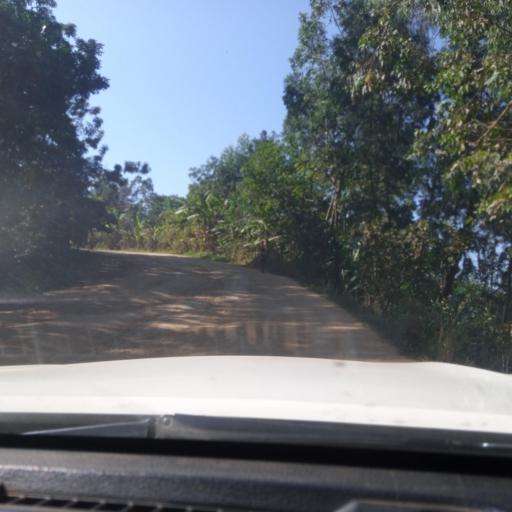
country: ET
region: Southern Nations, Nationalities, and People's Region
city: Mizan Teferi
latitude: 7.0093
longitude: 35.5534
